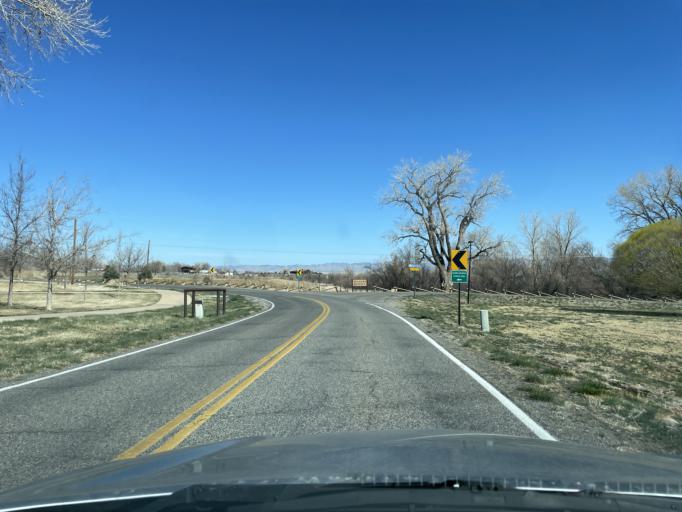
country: US
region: Colorado
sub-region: Mesa County
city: Redlands
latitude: 39.0770
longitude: -108.6640
